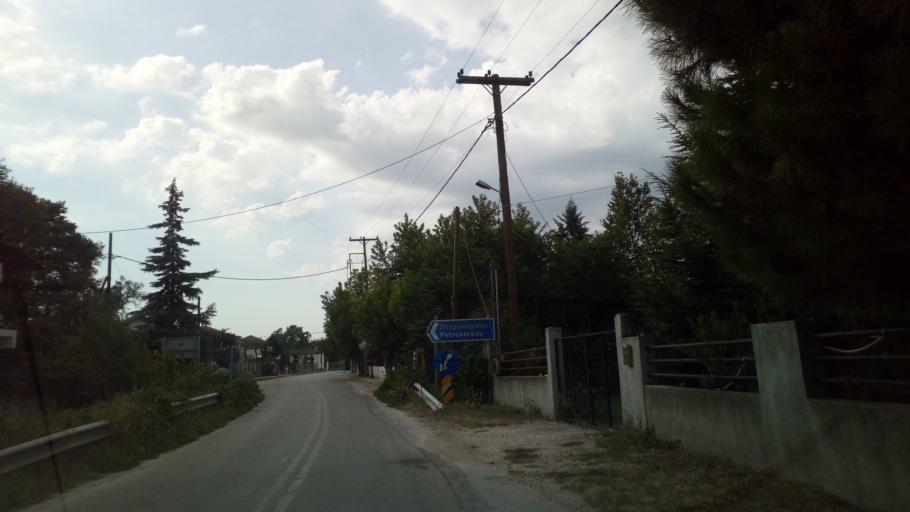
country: GR
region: Central Macedonia
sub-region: Nomos Thessalonikis
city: Gerakarou
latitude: 40.5673
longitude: 23.2882
